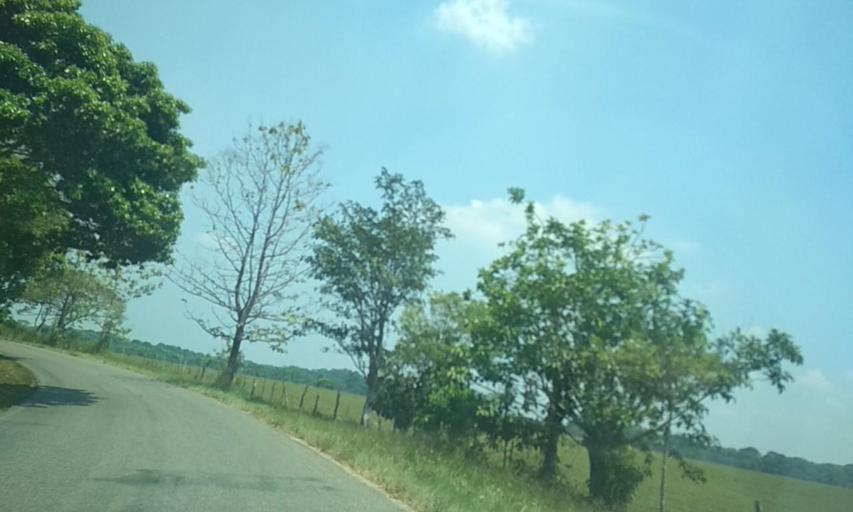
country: MX
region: Tabasco
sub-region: Cardenas
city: Poblado C-33 20 de Noviembre
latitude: 17.8407
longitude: -93.5604
